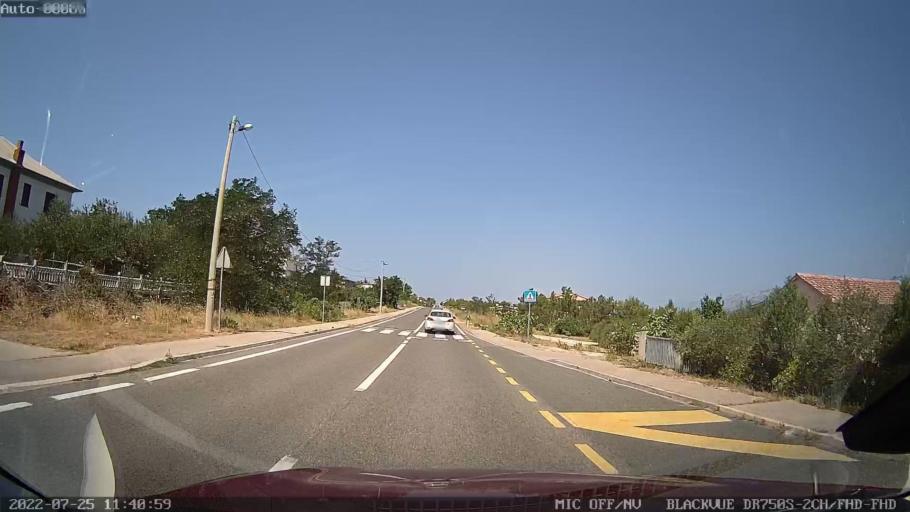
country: HR
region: Zadarska
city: Razanac
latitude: 44.2663
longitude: 15.3525
